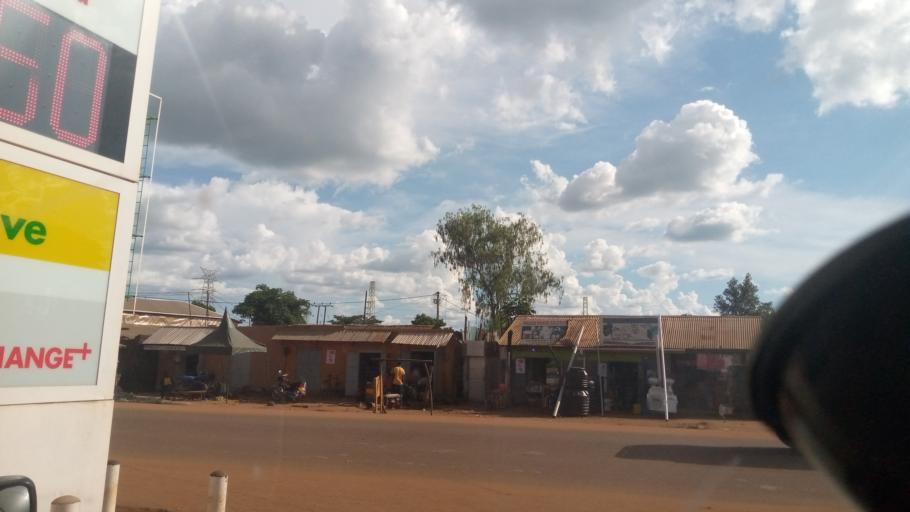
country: UG
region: Northern Region
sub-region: Lira District
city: Lira
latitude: 2.2440
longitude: 32.8868
